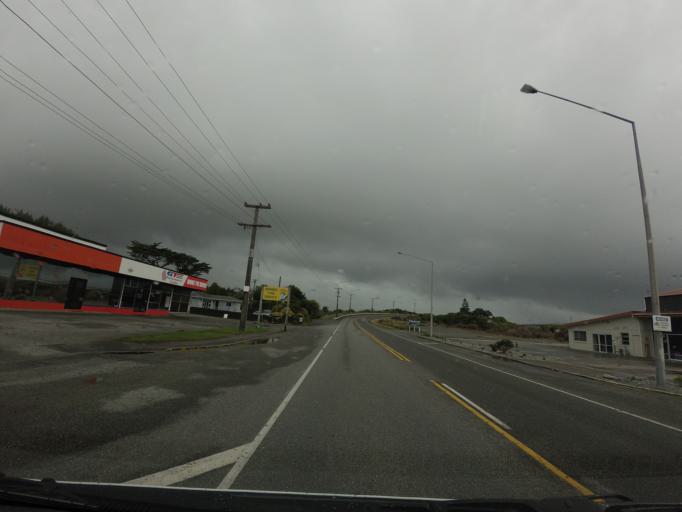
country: NZ
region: West Coast
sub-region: Grey District
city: Greymouth
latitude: -42.4891
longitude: 171.1799
